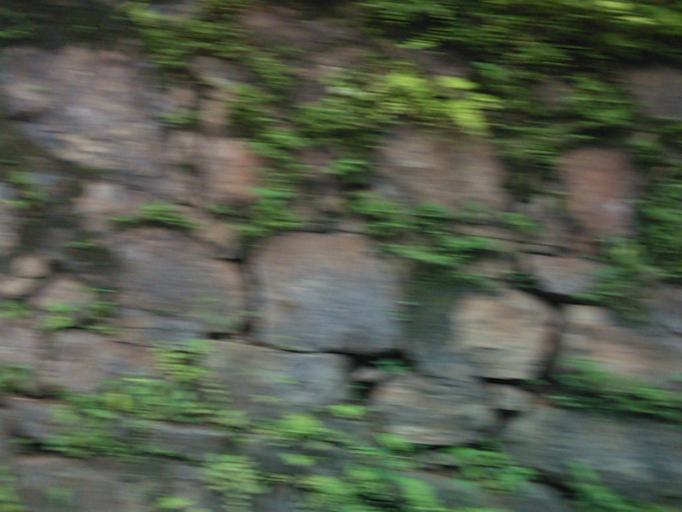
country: IN
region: Kerala
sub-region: Kozhikode
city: Kozhikode
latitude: 11.2878
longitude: 75.8123
